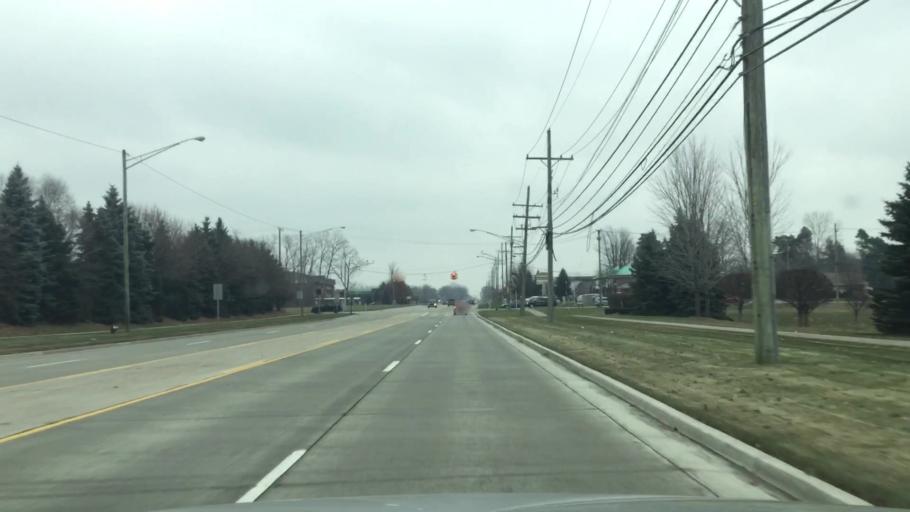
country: US
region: Michigan
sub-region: Macomb County
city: Fraser
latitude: 42.5530
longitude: -82.9722
